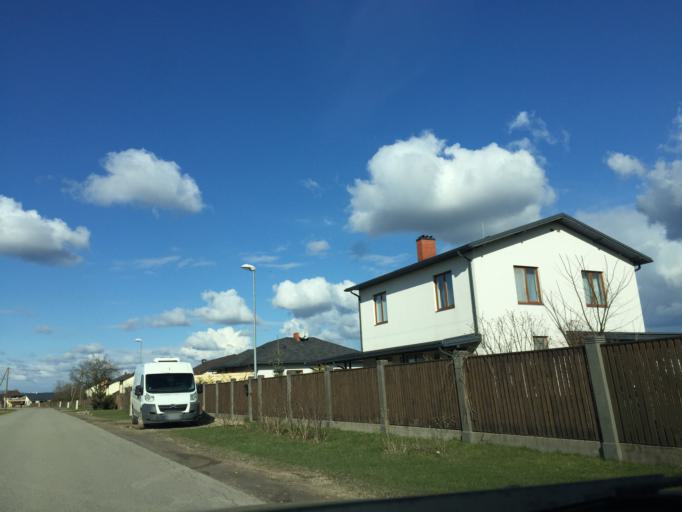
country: LV
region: Kekava
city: Kekava
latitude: 56.8367
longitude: 24.2079
